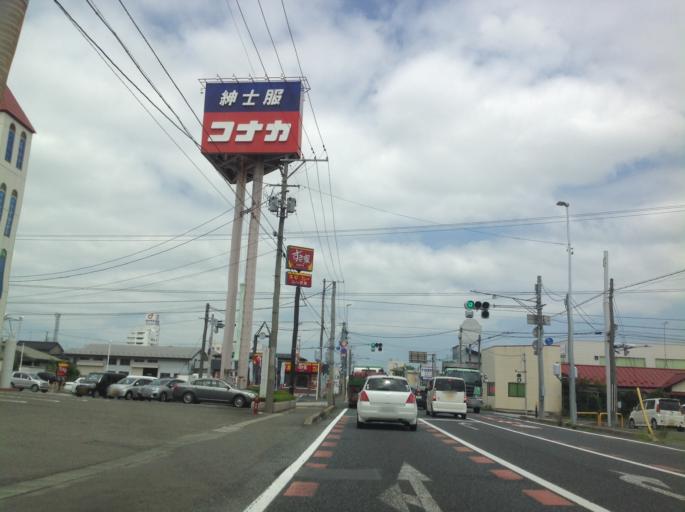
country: JP
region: Iwate
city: Mizusawa
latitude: 39.1358
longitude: 141.1500
